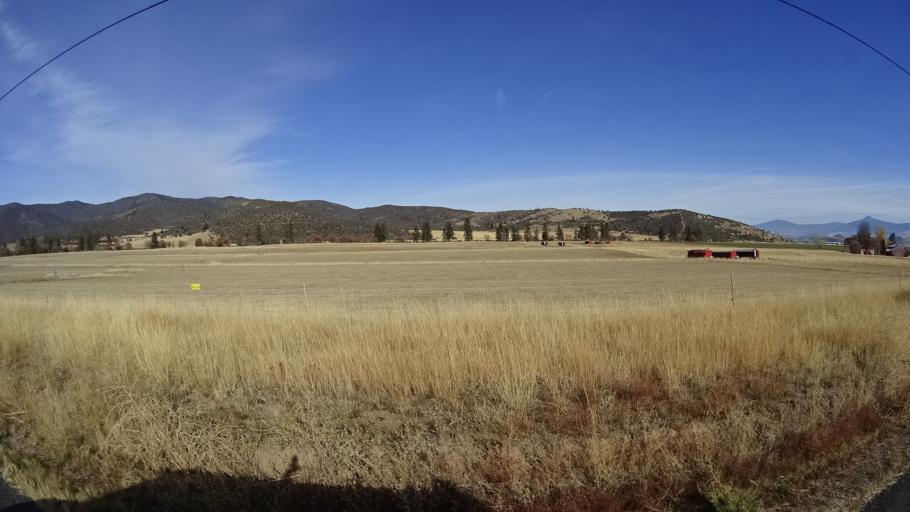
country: US
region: California
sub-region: Siskiyou County
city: Montague
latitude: 41.5388
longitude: -122.5783
